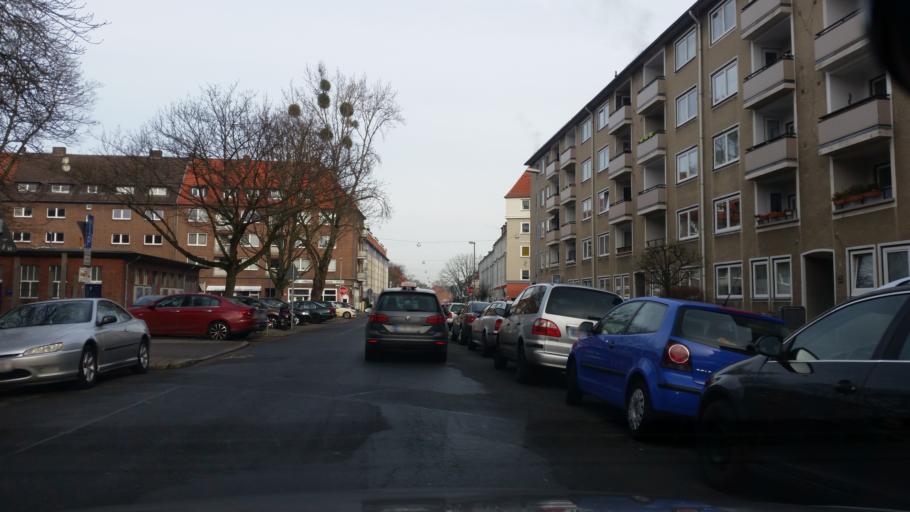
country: DE
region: Lower Saxony
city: Hannover
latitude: 52.3943
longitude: 9.7313
